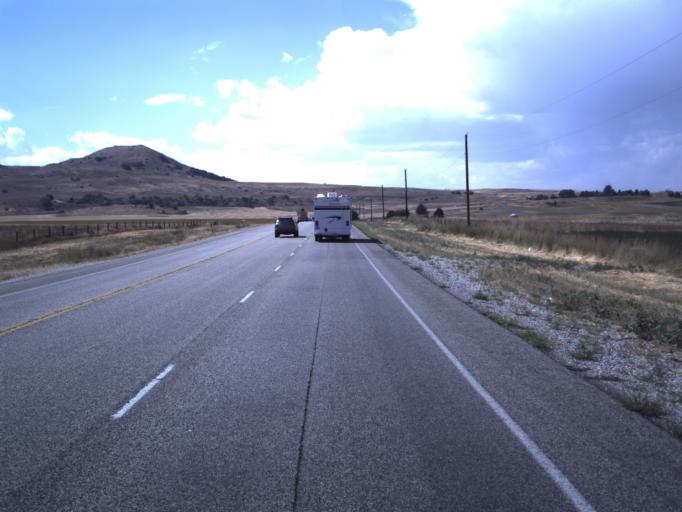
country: US
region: Utah
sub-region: Cache County
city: Mendon
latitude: 41.7538
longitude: -111.9921
